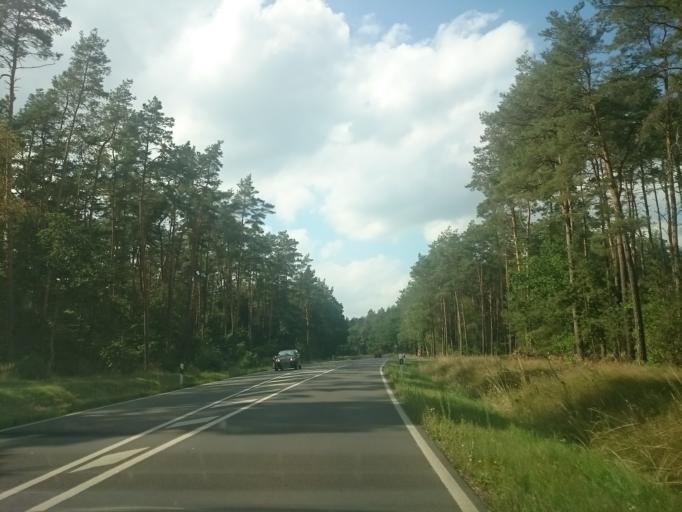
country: DE
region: Mecklenburg-Vorpommern
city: Torgelow
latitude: 53.6327
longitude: 13.9888
